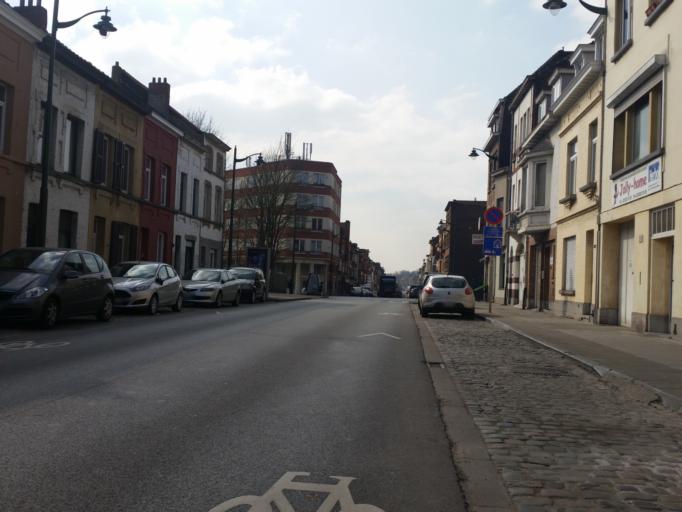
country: BE
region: Brussels Capital
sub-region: Bruxelles-Capitale
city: Brussels
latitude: 50.8420
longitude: 4.3166
